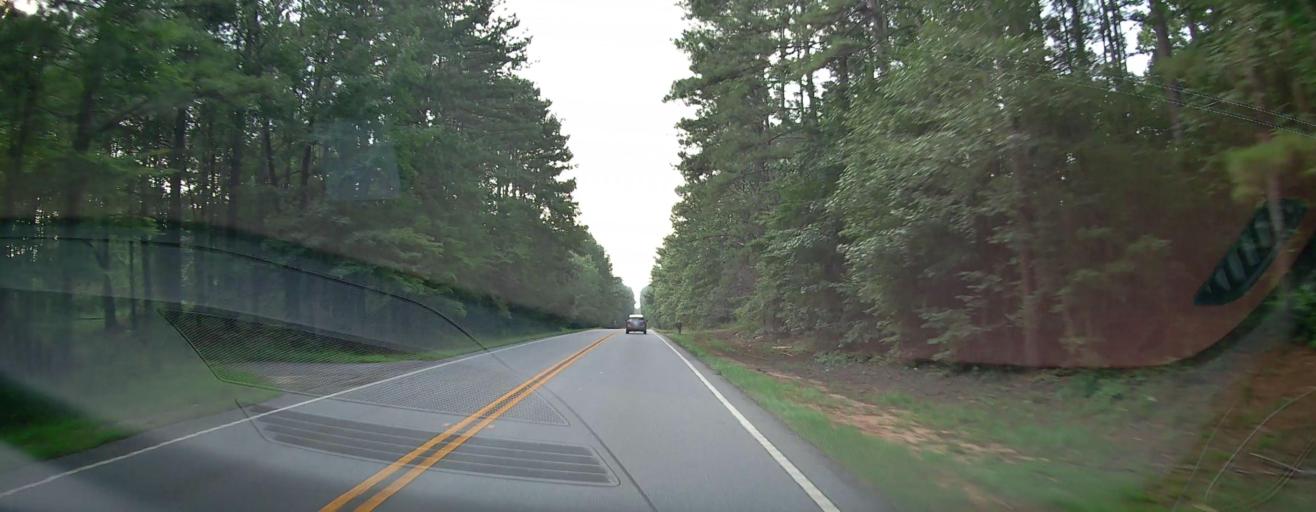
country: US
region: Georgia
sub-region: Monroe County
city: Forsyth
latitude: 33.0463
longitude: -83.7592
